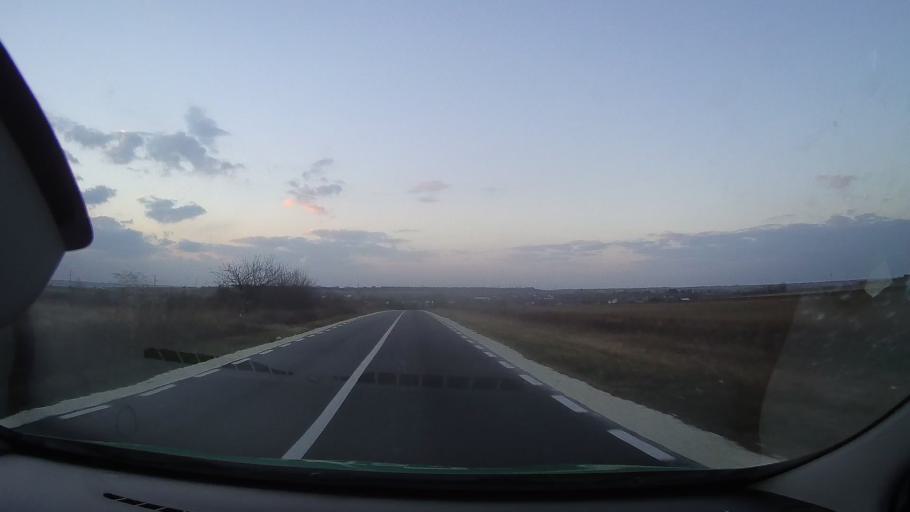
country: RO
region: Constanta
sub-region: Comuna Baneasa
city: Baneasa
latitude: 44.0960
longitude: 27.6824
